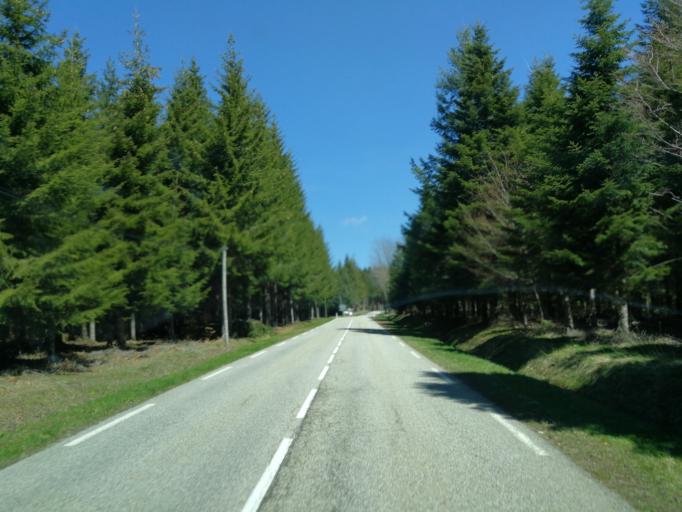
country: FR
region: Rhone-Alpes
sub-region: Departement de l'Ardeche
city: Saint-Agreve
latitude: 45.0360
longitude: 4.4109
